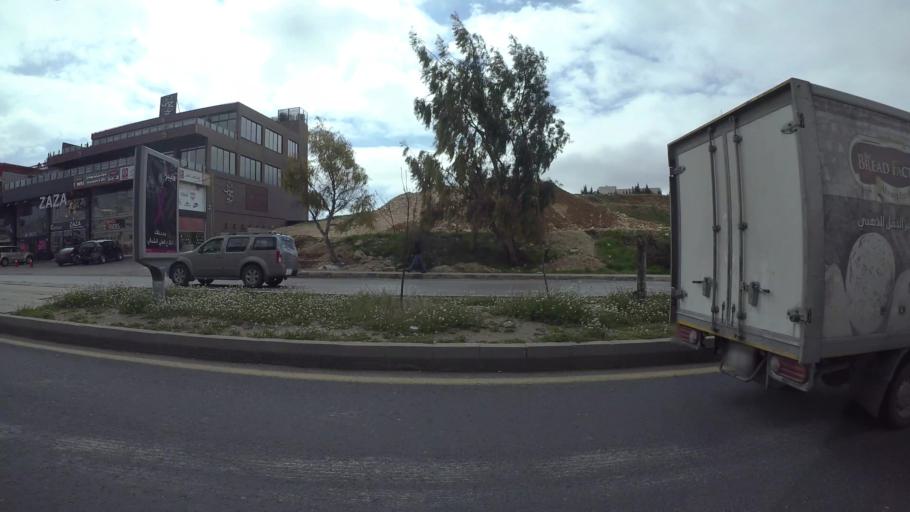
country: JO
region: Amman
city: Al Jubayhah
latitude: 31.9961
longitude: 35.8345
